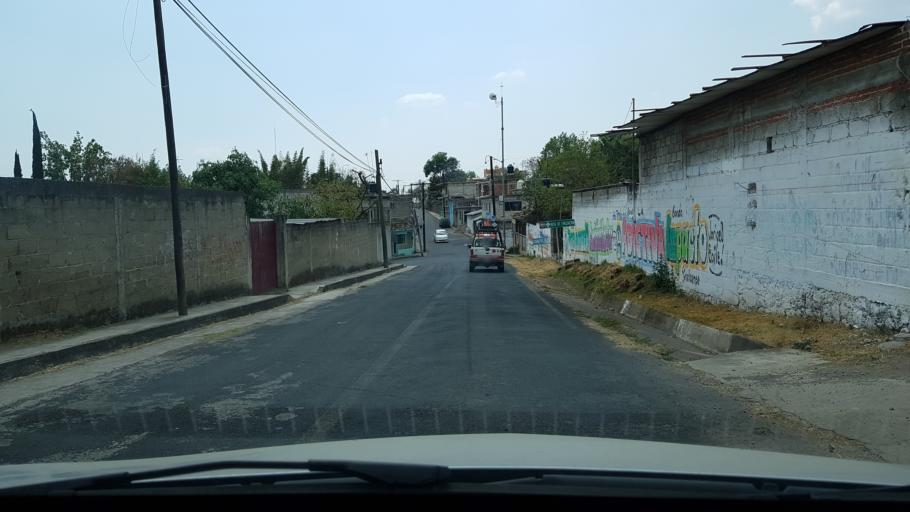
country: MX
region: Morelos
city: Tlacotepec
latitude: 18.8164
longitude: -98.7473
